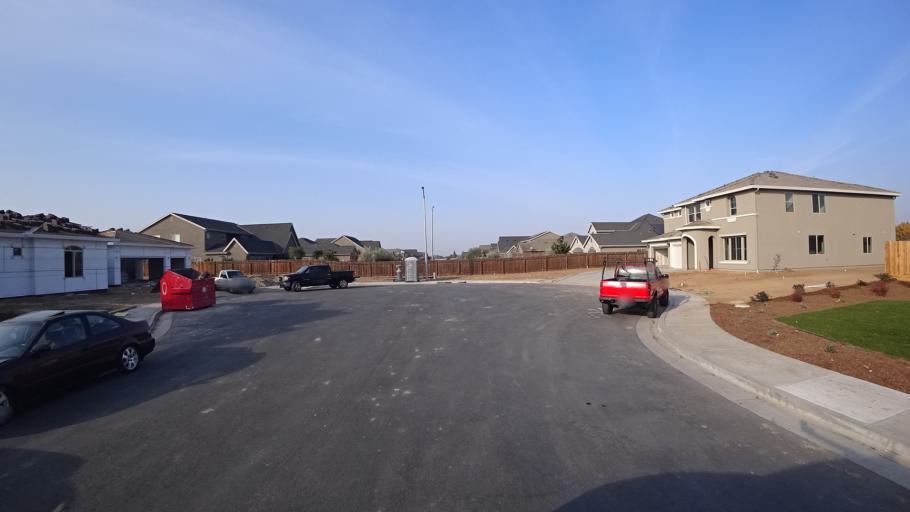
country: US
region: California
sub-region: Kern County
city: Greenacres
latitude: 35.4329
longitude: -119.1052
